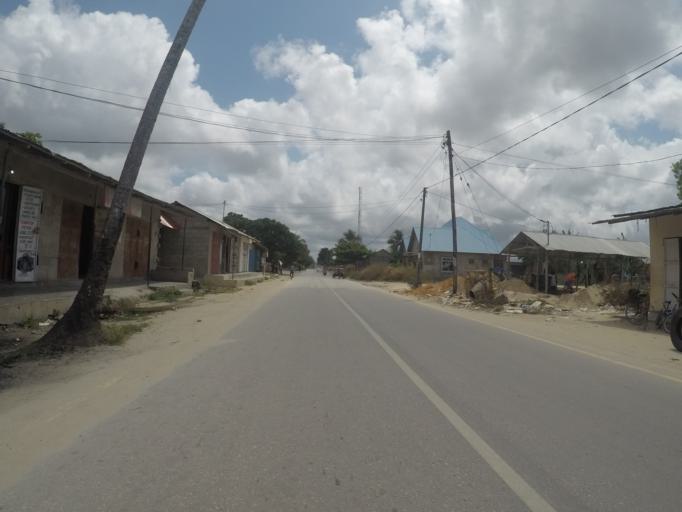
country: TZ
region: Zanzibar Urban/West
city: Zanzibar
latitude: -6.1980
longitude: 39.2439
